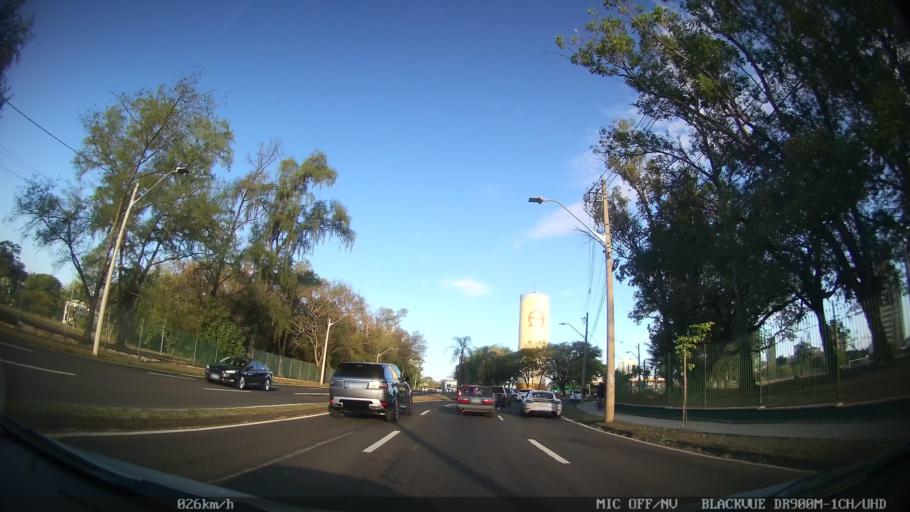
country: BR
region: Sao Paulo
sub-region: Piracicaba
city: Piracicaba
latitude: -22.7140
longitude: -47.6330
